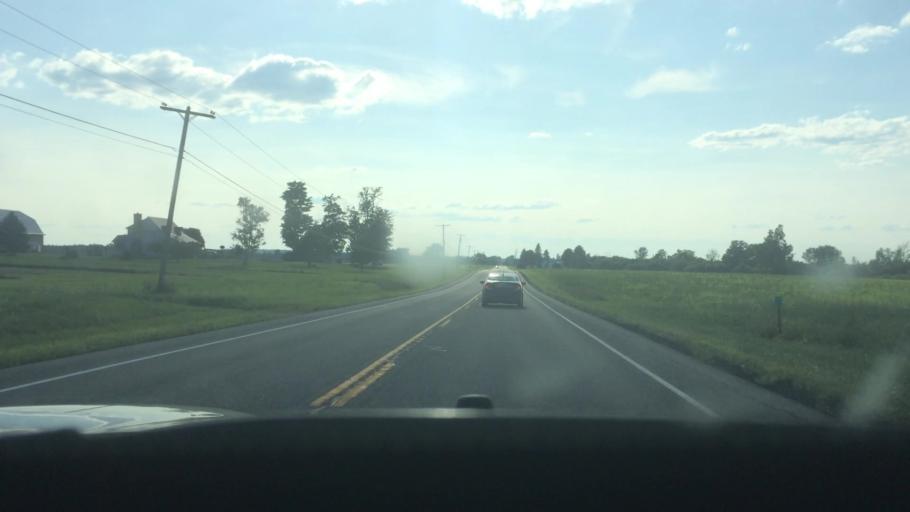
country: US
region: New York
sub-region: St. Lawrence County
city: Potsdam
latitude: 44.6890
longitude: -74.7555
